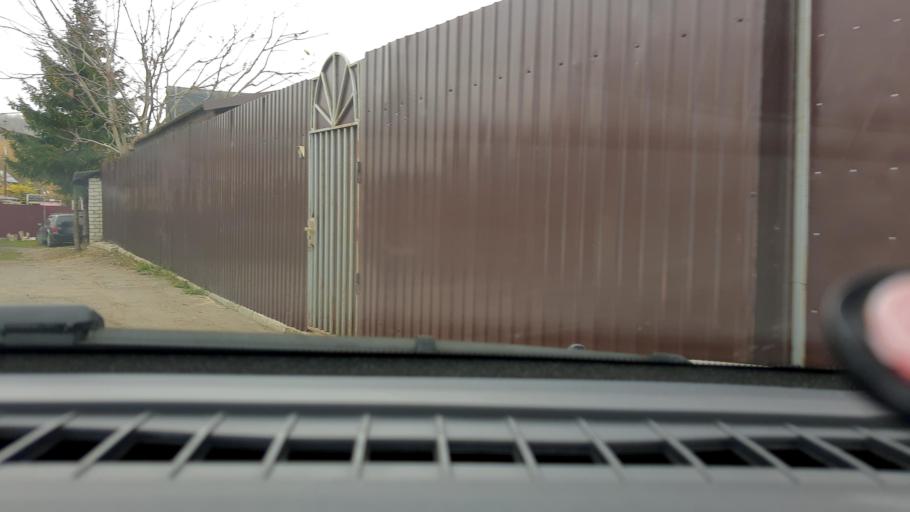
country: RU
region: Nizjnij Novgorod
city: Nizhniy Novgorod
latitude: 56.2707
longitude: 43.9572
